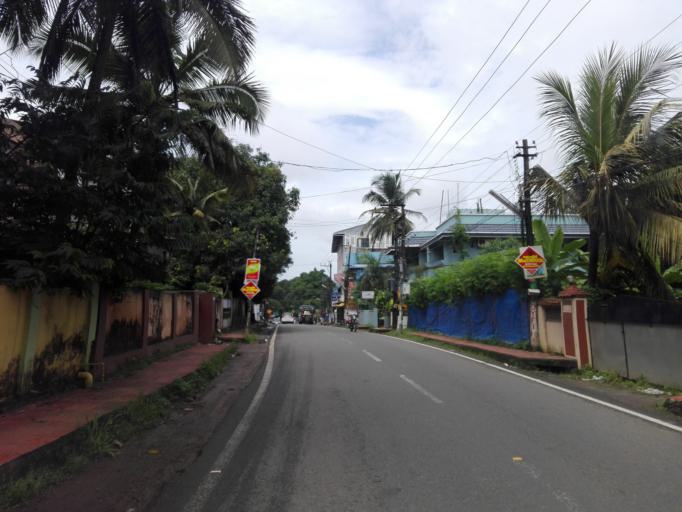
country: IN
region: Kerala
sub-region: Ernakulam
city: Elur
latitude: 10.0223
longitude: 76.3389
